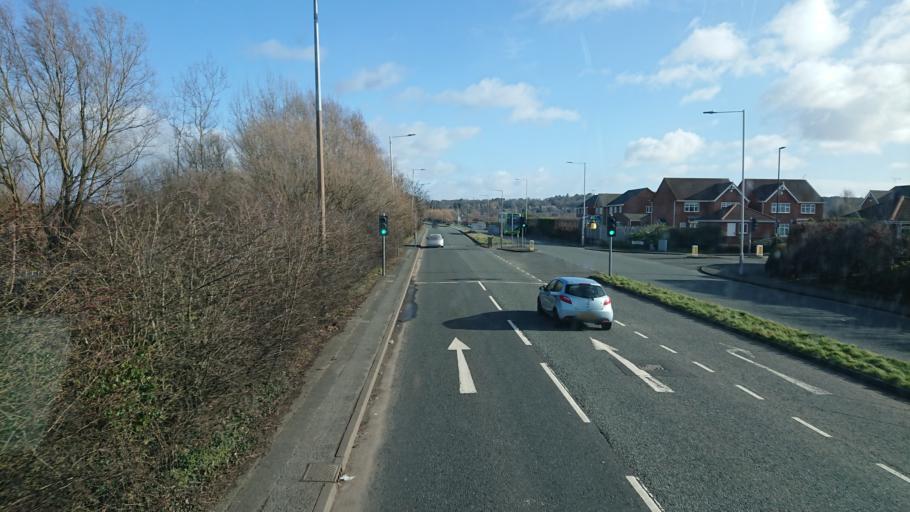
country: GB
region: England
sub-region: Metropolitan Borough of Wirral
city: Moreton
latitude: 53.4049
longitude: -3.0959
